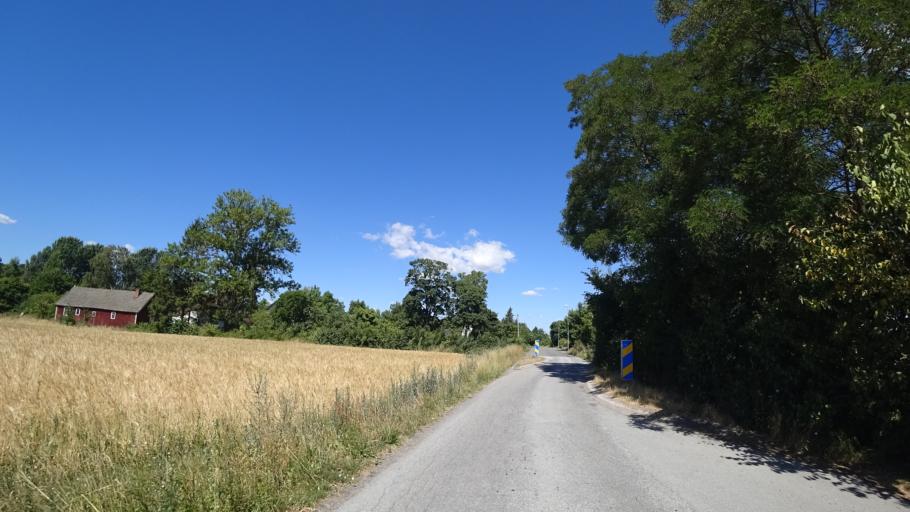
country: SE
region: Skane
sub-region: Kristianstads Kommun
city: Onnestad
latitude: 56.0423
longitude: 14.0354
